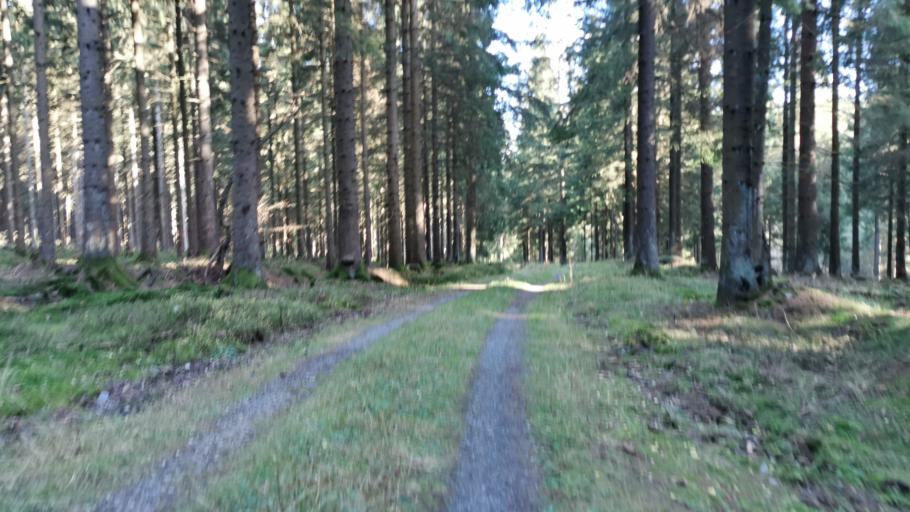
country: DE
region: Bavaria
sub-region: Upper Franconia
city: Reichenbach
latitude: 50.4437
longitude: 11.4251
